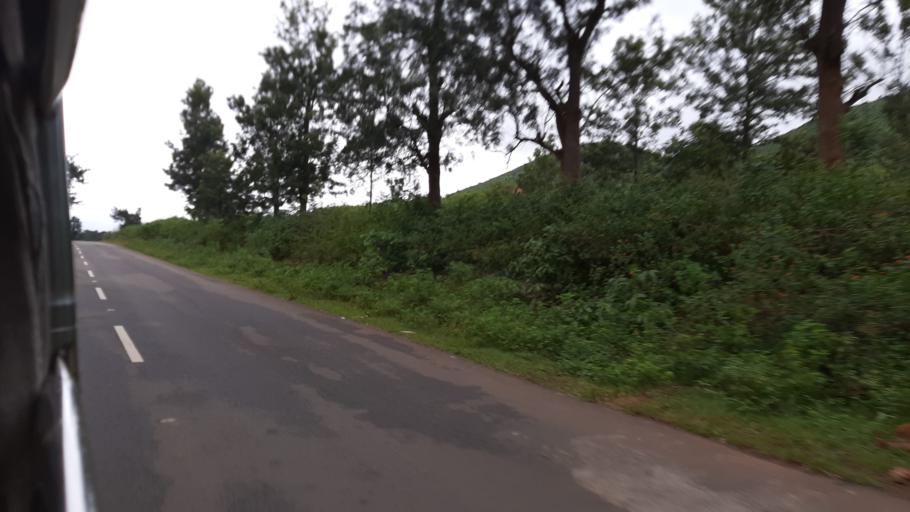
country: IN
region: Andhra Pradesh
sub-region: Vizianagaram District
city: Salur
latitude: 18.2890
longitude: 82.9275
